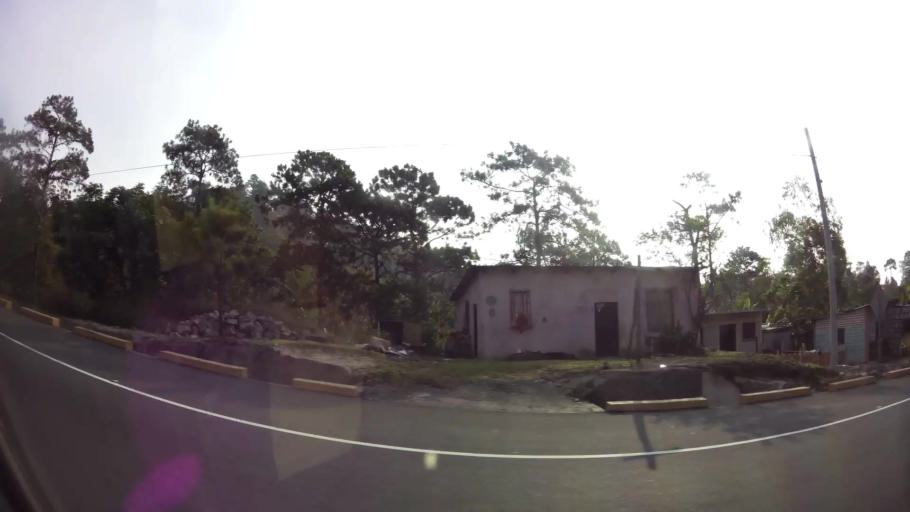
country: HN
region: Francisco Morazan
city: Zambrano
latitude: 14.2678
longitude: -87.3997
